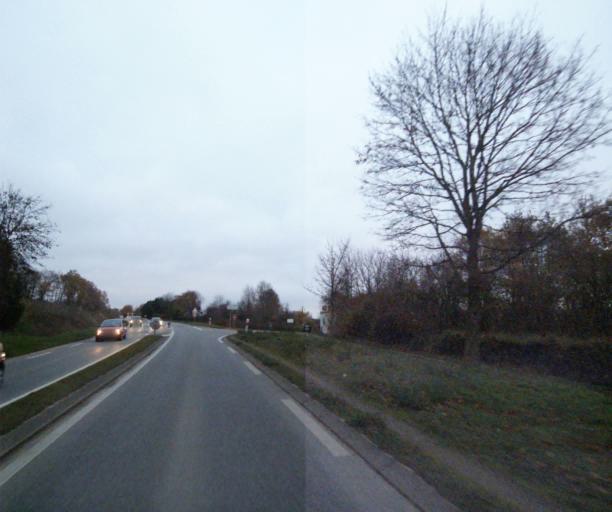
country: FR
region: Ile-de-France
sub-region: Departement des Yvelines
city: Villennes-sur-Seine
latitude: 48.9474
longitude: 1.9794
